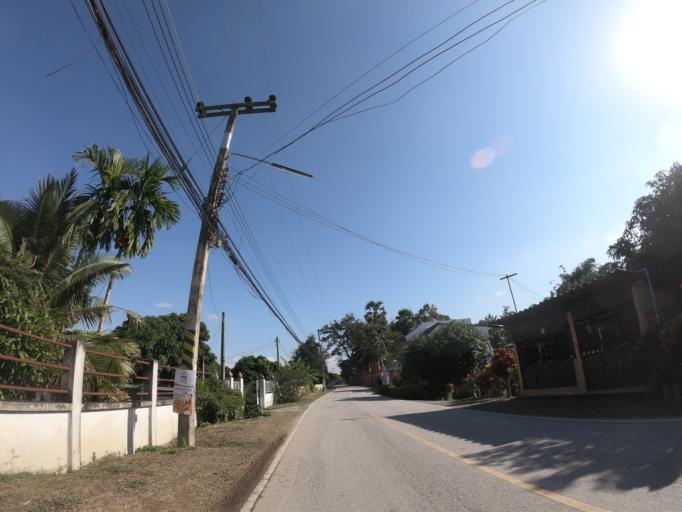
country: TH
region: Chiang Mai
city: Saraphi
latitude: 18.6982
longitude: 98.9950
